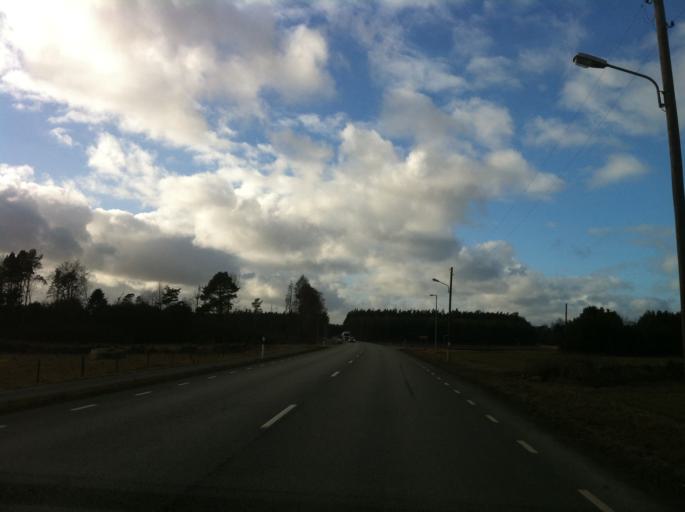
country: SE
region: Skane
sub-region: Bromolla Kommun
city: Bromoella
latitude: 56.0627
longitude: 14.5177
